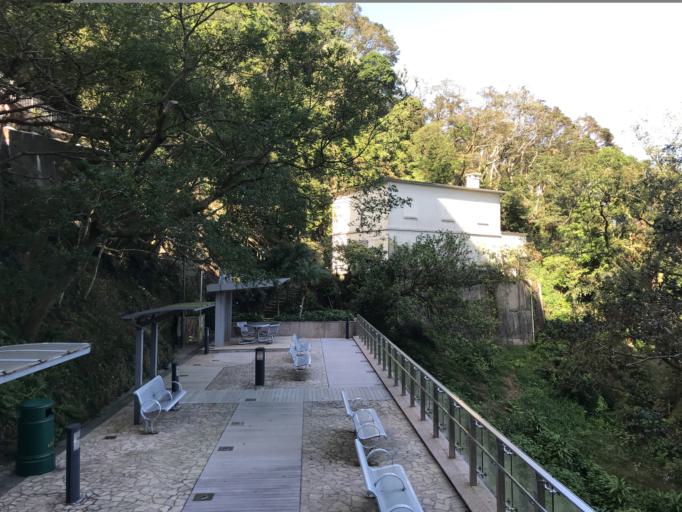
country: HK
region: Central and Western
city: Central
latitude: 22.2715
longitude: 114.1499
